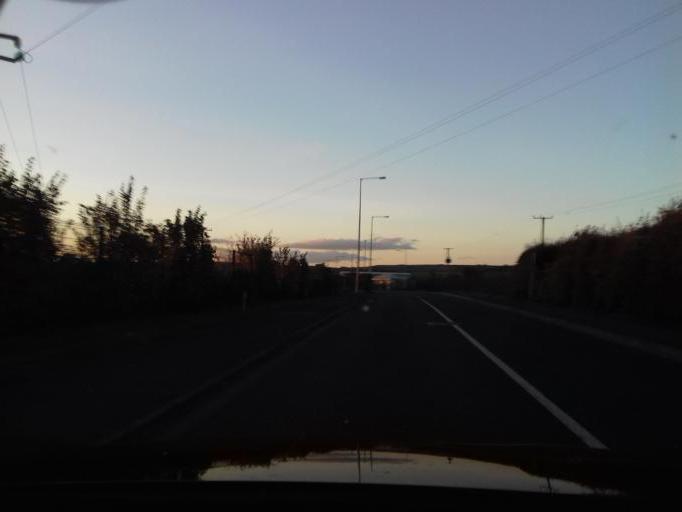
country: IE
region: Leinster
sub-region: Lu
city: Drogheda
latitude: 53.7217
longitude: -6.3777
